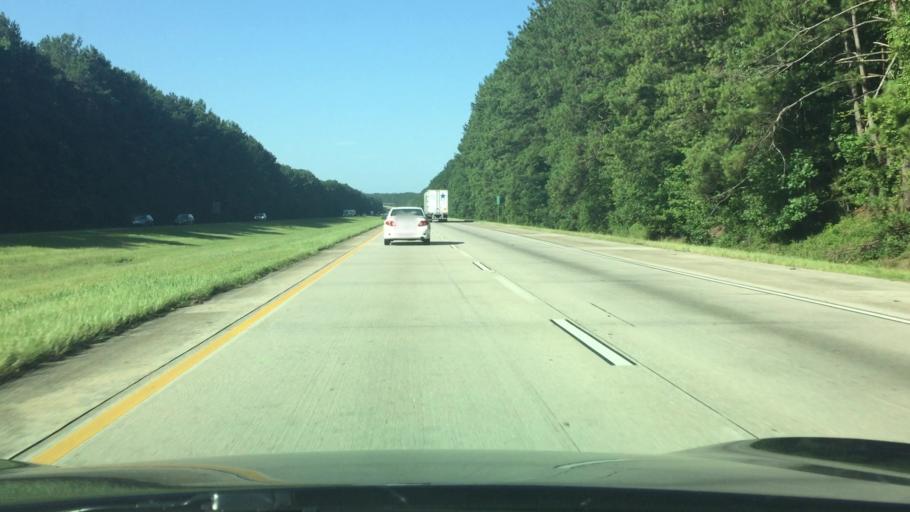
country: US
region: Georgia
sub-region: Troup County
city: Hogansville
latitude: 33.1442
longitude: -84.8811
